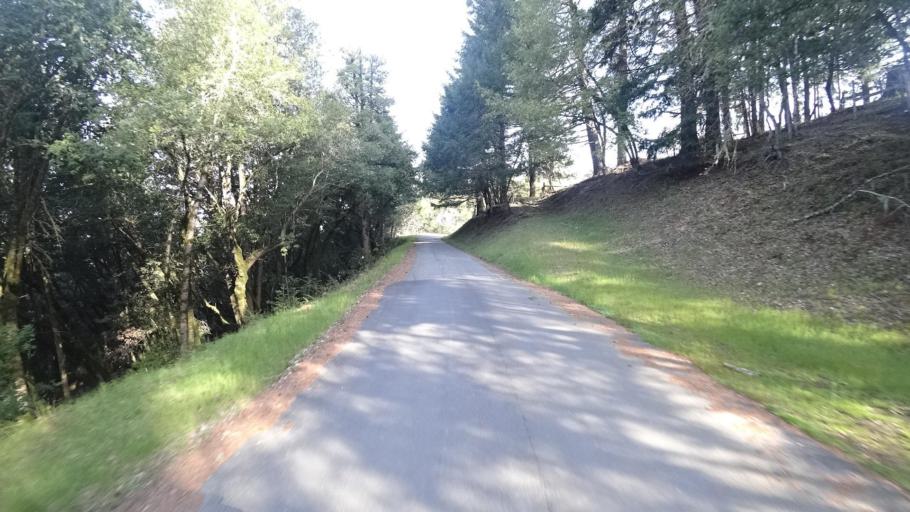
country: US
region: California
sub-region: Humboldt County
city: Hydesville
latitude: 40.6488
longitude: -123.9236
